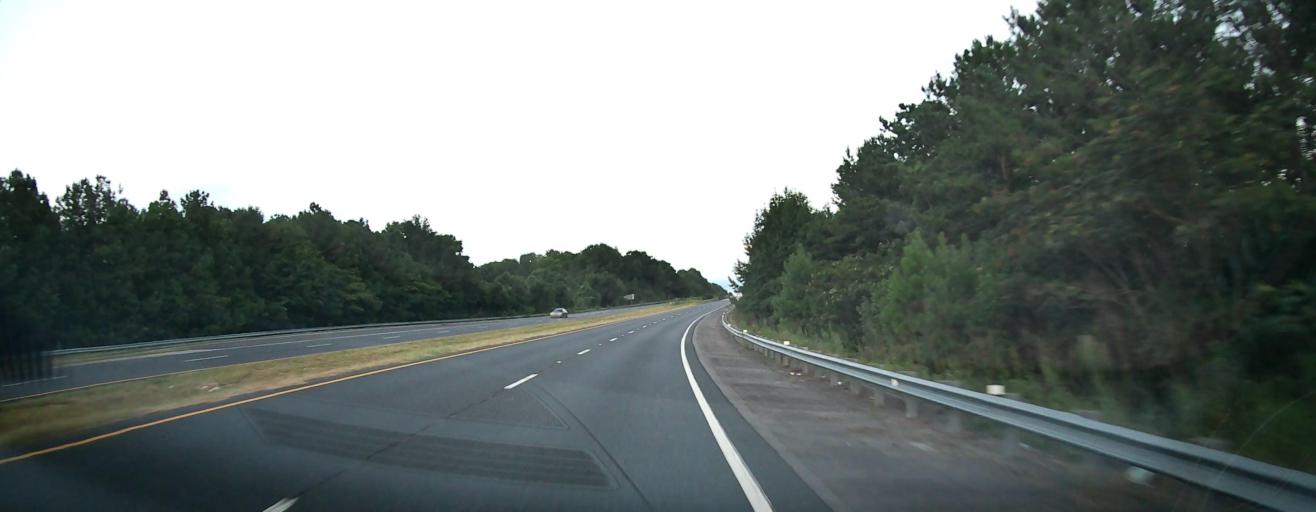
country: US
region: Georgia
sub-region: Muscogee County
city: Columbus
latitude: 32.5199
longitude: -84.9120
